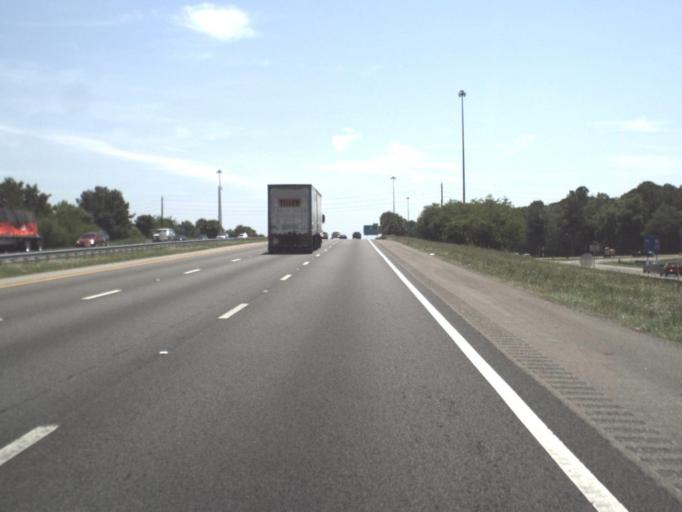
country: US
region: Florida
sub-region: Clay County
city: Bellair-Meadowbrook Terrace
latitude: 30.2724
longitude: -81.7684
